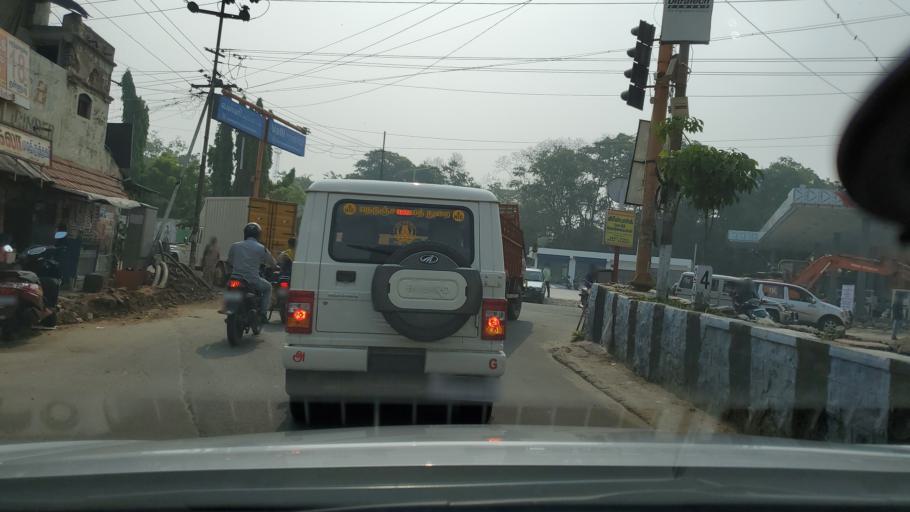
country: IN
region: Tamil Nadu
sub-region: Erode
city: Erode
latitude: 11.3293
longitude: 77.7238
